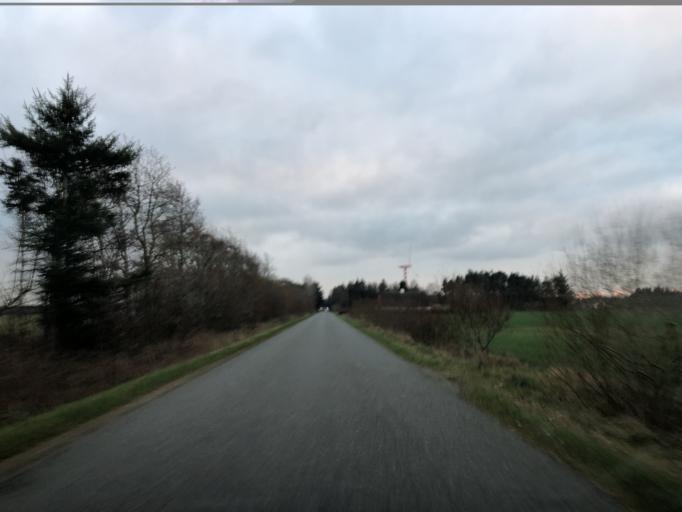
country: DK
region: Central Jutland
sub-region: Holstebro Kommune
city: Ulfborg
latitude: 56.2619
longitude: 8.2848
